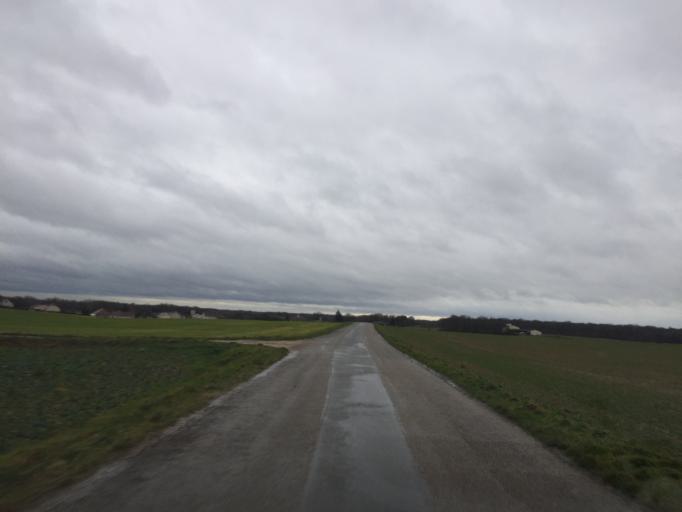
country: FR
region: Franche-Comte
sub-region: Departement du Jura
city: Champvans
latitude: 47.1520
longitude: 5.4657
